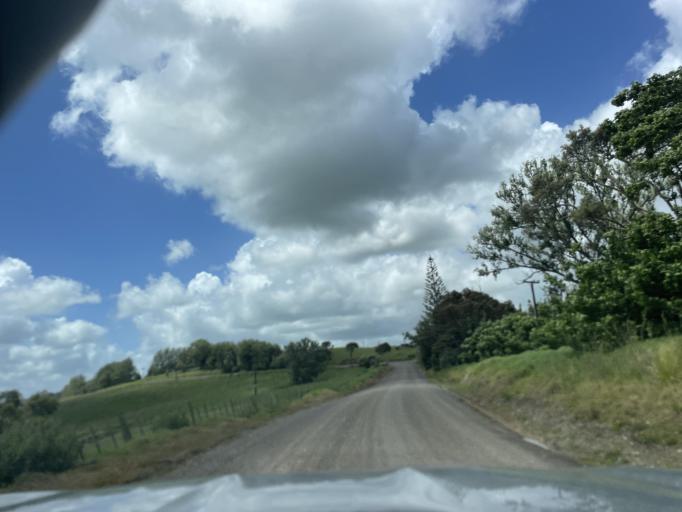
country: NZ
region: Auckland
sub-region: Auckland
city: Wellsford
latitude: -36.1695
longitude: 174.3191
